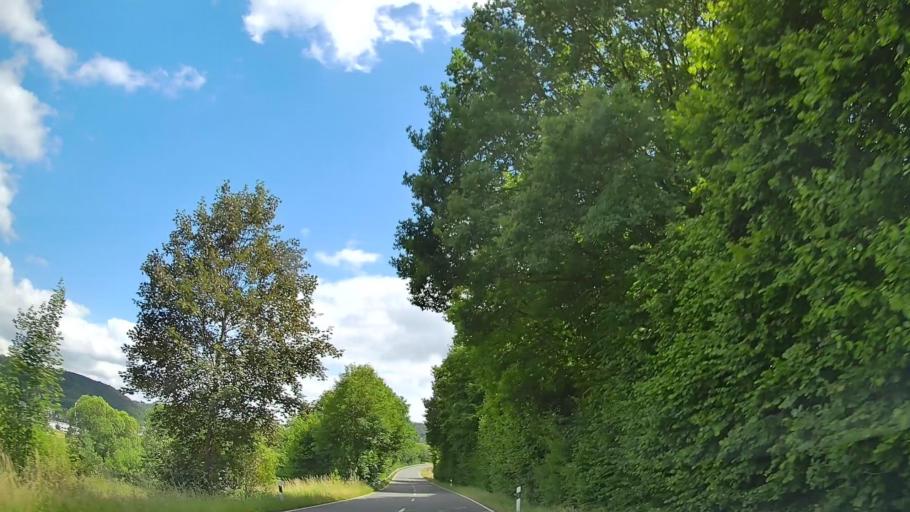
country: DE
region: North Rhine-Westphalia
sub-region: Regierungsbezirk Detmold
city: Lugde
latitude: 51.9651
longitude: 9.2364
